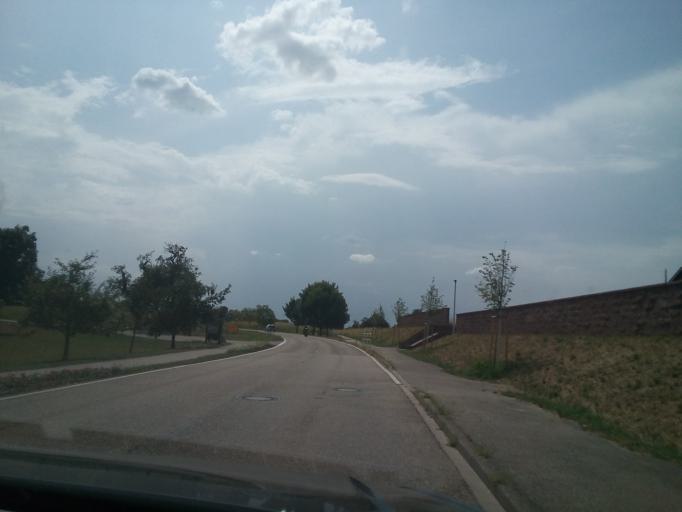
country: DE
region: Baden-Wuerttemberg
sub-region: Karlsruhe Region
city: Kuppenheim
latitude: 48.8234
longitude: 8.2345
